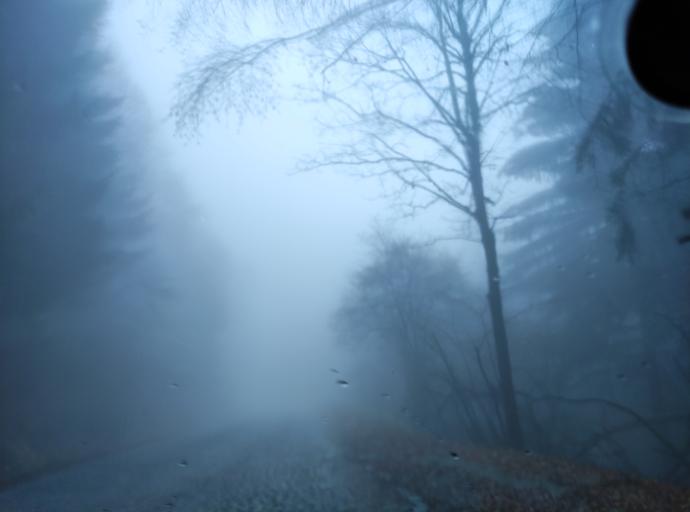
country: BG
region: Sofia-Capital
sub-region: Stolichna Obshtina
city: Sofia
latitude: 42.6154
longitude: 23.2953
